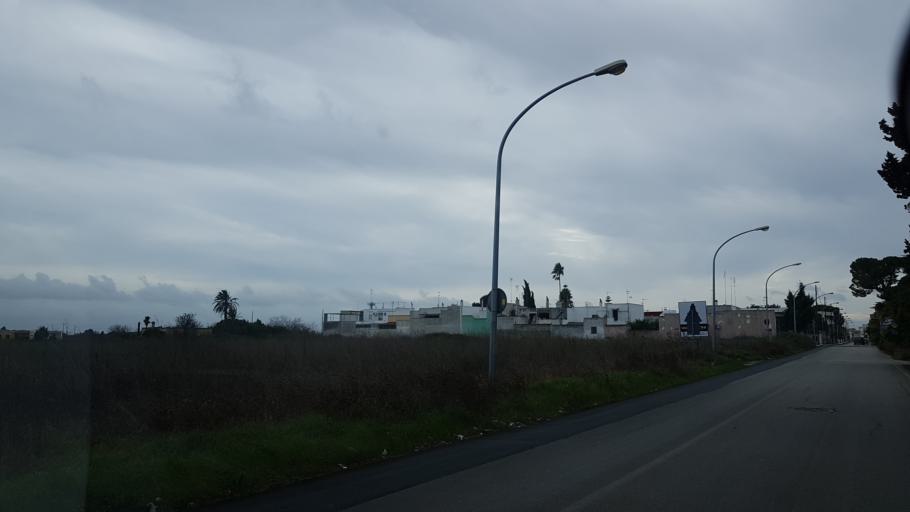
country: IT
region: Apulia
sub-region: Provincia di Brindisi
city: Mesagne
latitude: 40.5680
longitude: 17.8000
